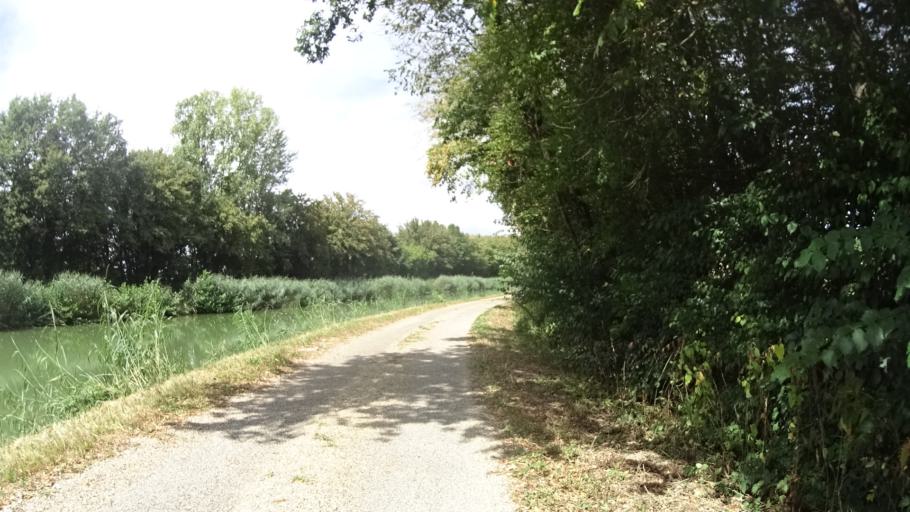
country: FR
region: Franche-Comte
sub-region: Departement du Jura
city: Saint-Aubin
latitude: 47.0928
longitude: 5.3257
